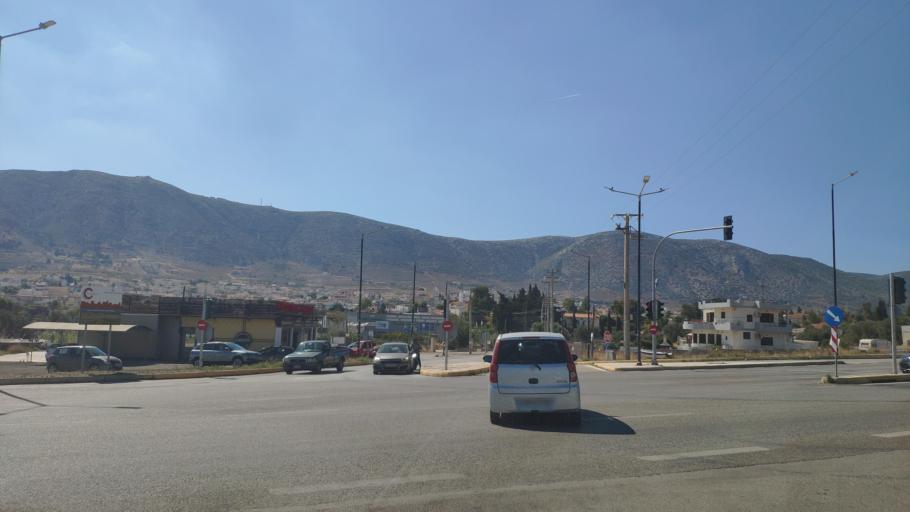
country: GR
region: Attica
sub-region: Nomarchia Anatolikis Attikis
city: Keratea
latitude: 37.8124
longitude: 23.9838
